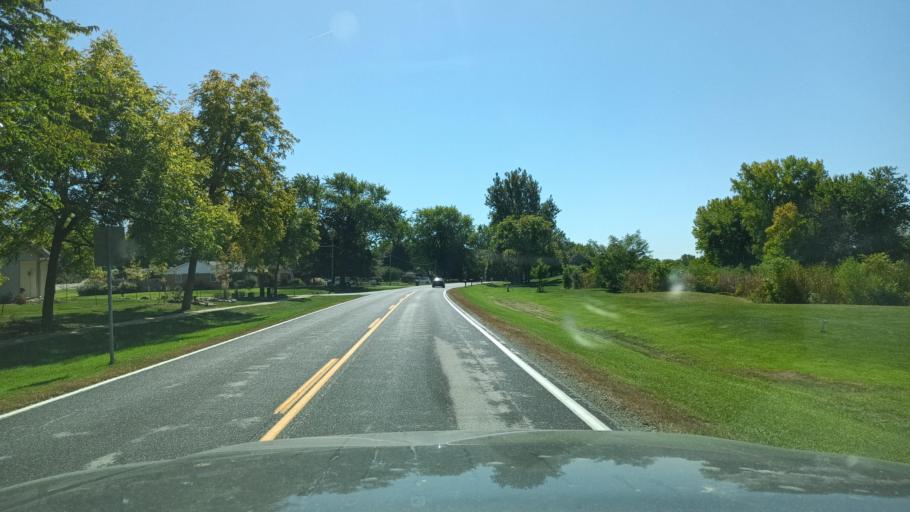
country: US
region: Illinois
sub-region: Champaign County
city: Lake of the Woods
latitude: 40.2043
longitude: -88.3710
